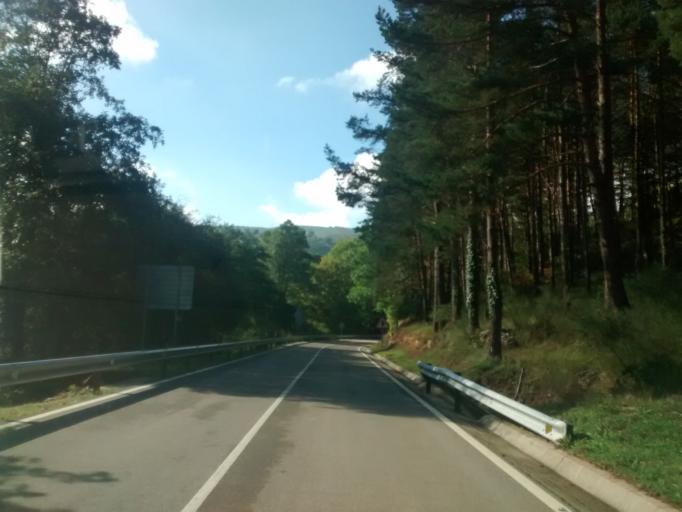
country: ES
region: Cantabria
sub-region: Provincia de Cantabria
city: Reinosa
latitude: 42.9423
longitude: -4.0474
